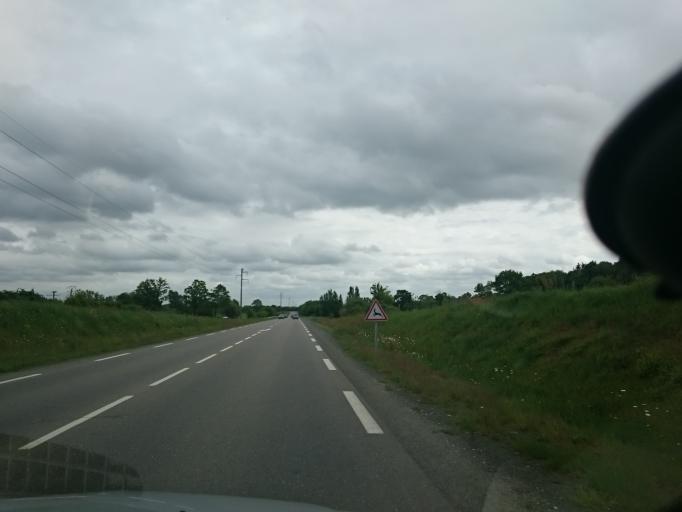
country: FR
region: Brittany
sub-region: Departement d'Ille-et-Vilaine
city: Saint-Brice-en-Cogles
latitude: 48.4079
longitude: -1.3815
